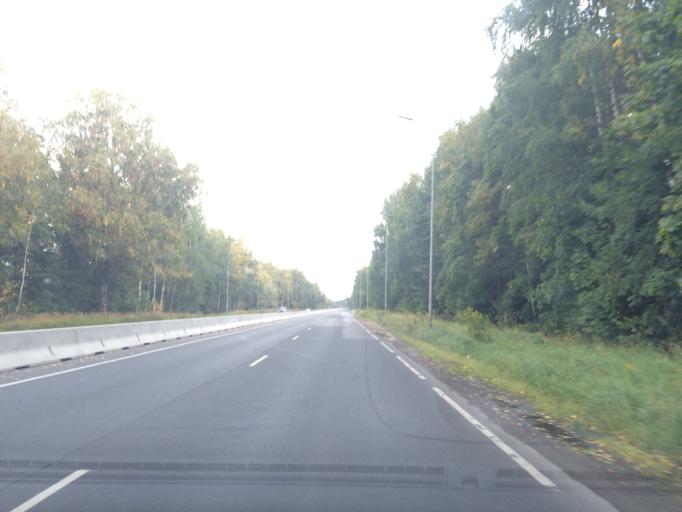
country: LV
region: Kekava
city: Kekava
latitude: 56.8750
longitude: 24.2627
